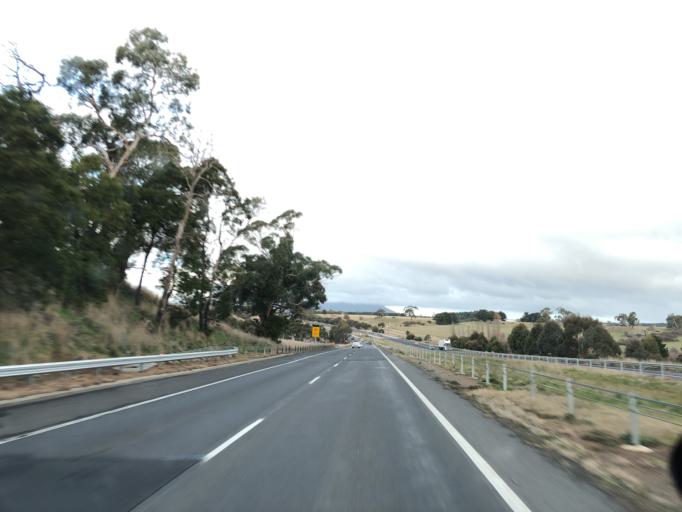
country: AU
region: Victoria
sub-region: Mount Alexander
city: Castlemaine
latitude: -37.2675
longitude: 144.4755
